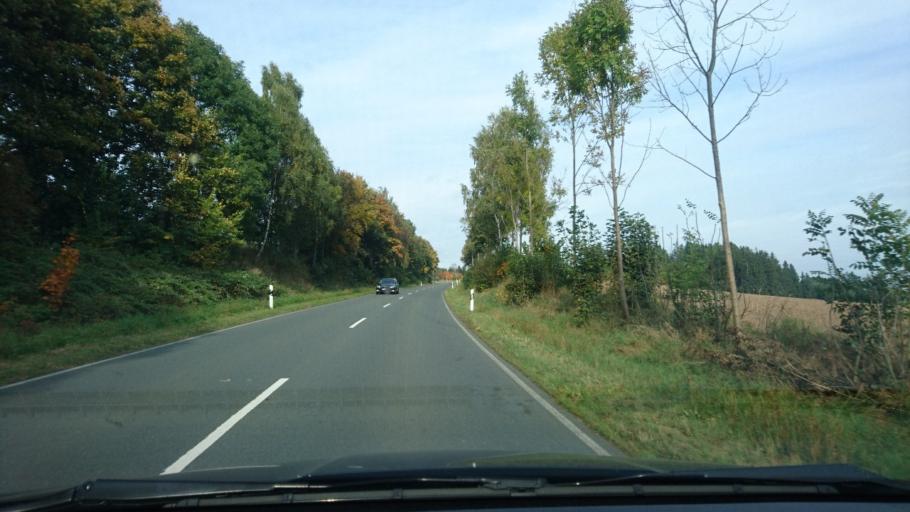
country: DE
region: Bavaria
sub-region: Upper Franconia
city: Naila
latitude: 50.3255
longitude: 11.7227
